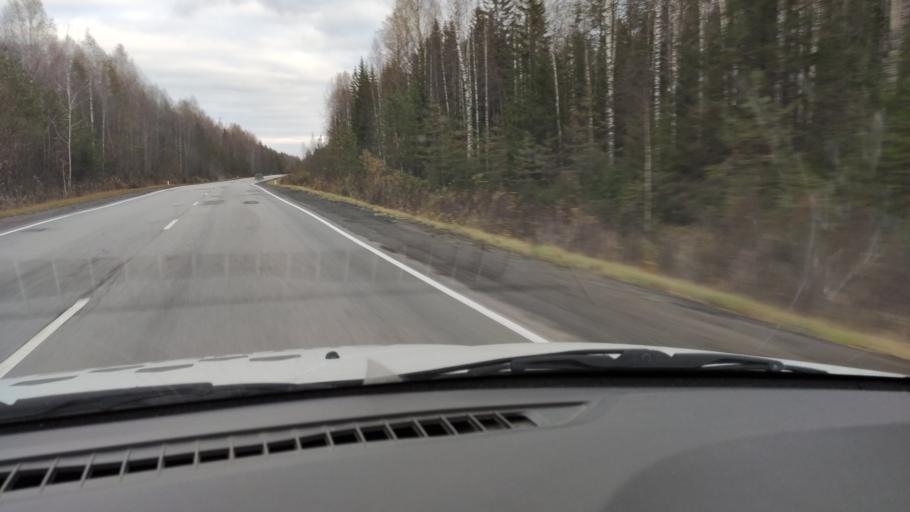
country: RU
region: Kirov
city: Chernaya Kholunitsa
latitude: 58.8683
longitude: 51.5602
